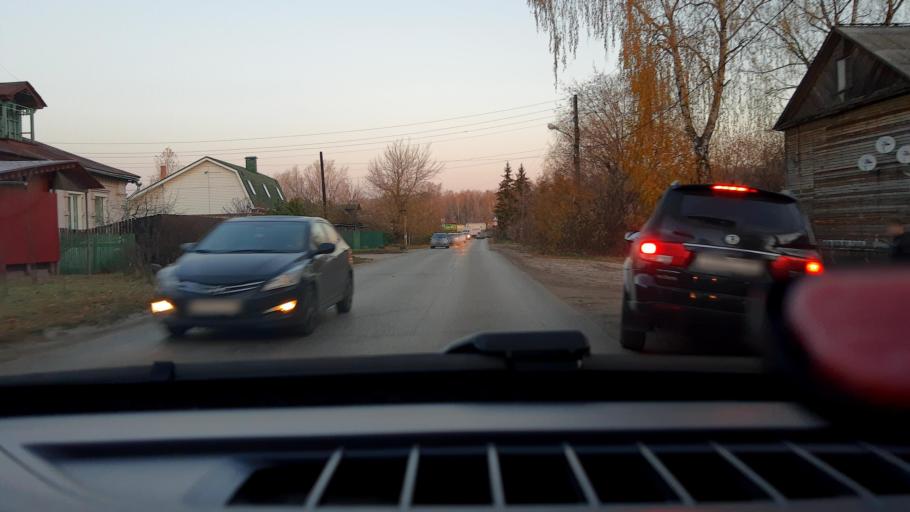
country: RU
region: Nizjnij Novgorod
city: Gorbatovka
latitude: 56.3454
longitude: 43.8295
